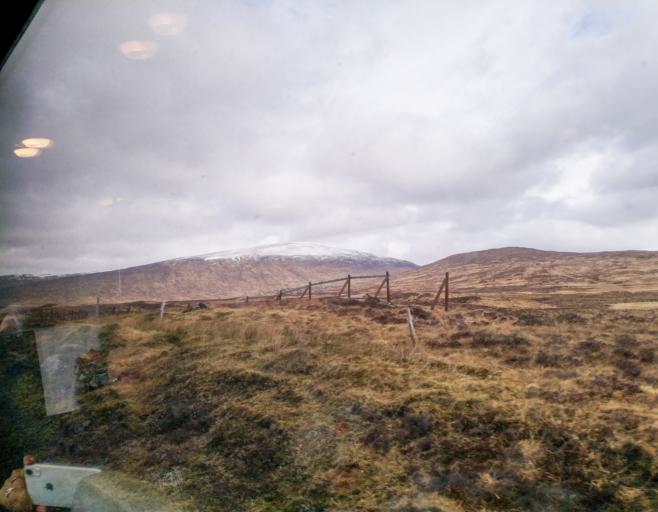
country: GB
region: Scotland
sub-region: Highland
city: Spean Bridge
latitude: 56.7427
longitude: -4.6678
